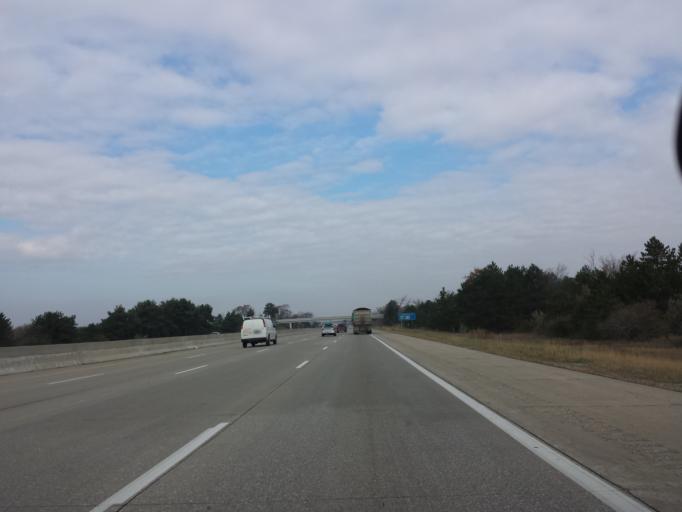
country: US
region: Michigan
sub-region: Saginaw County
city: Birch Run
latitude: 43.2327
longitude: -83.7690
